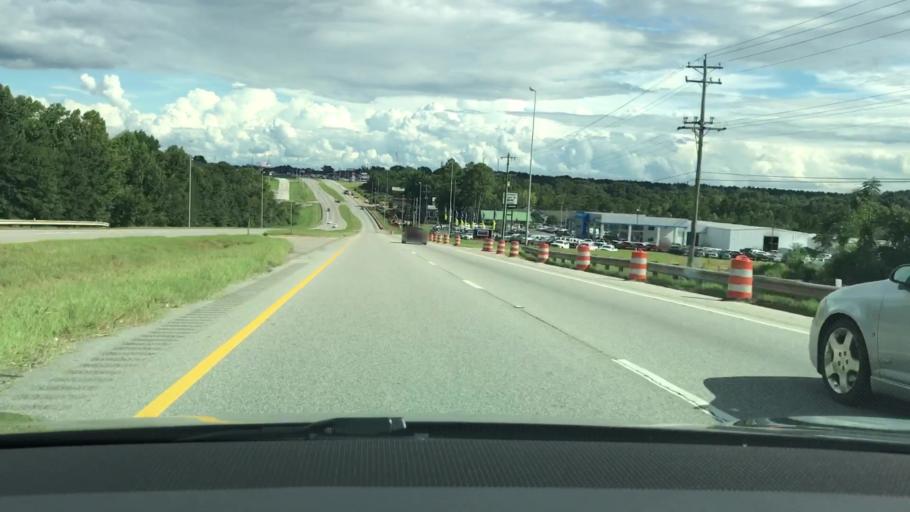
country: US
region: Alabama
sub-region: Pike County
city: Troy
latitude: 31.8016
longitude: -85.9853
